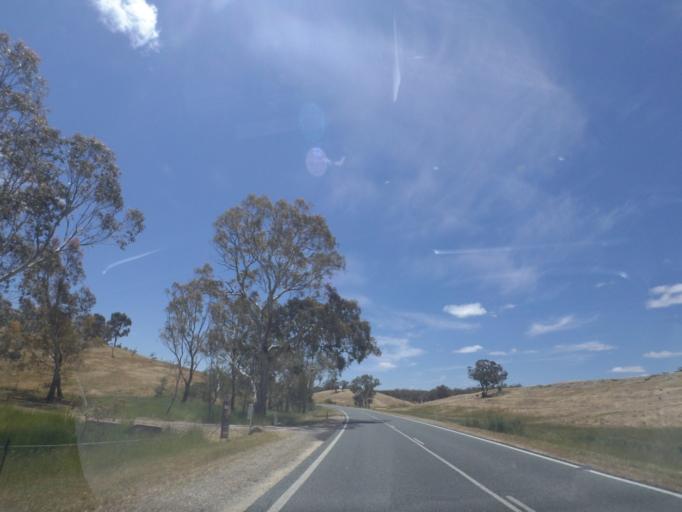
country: AU
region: Victoria
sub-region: Mount Alexander
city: Castlemaine
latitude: -37.1924
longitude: 144.1487
